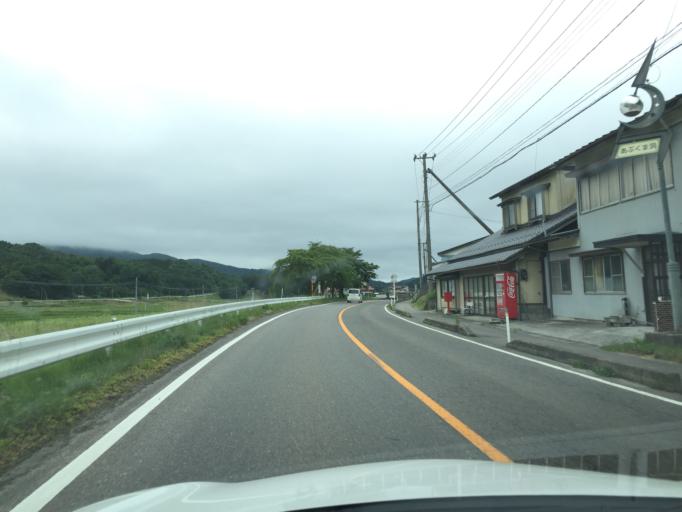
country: JP
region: Fukushima
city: Funehikimachi-funehiki
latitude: 37.3454
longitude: 140.6514
